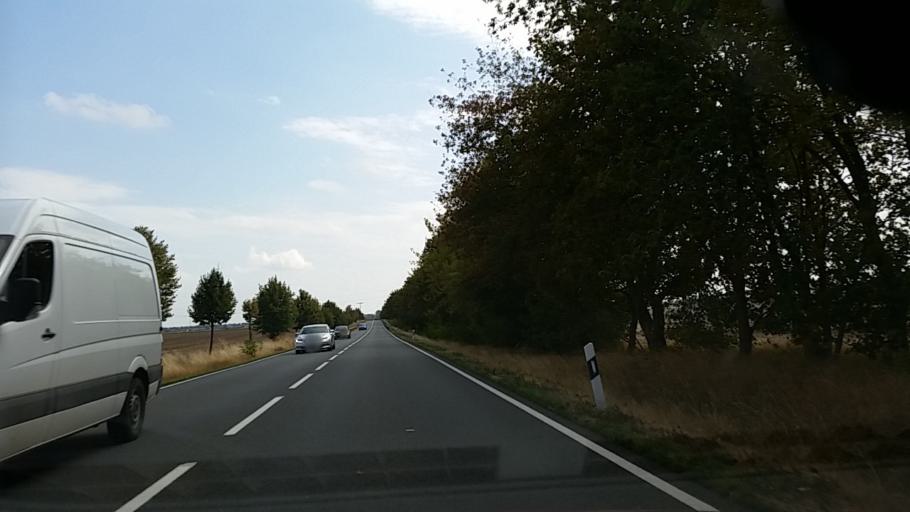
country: DE
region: Saxony-Anhalt
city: Querfurt
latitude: 51.3619
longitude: 11.6185
